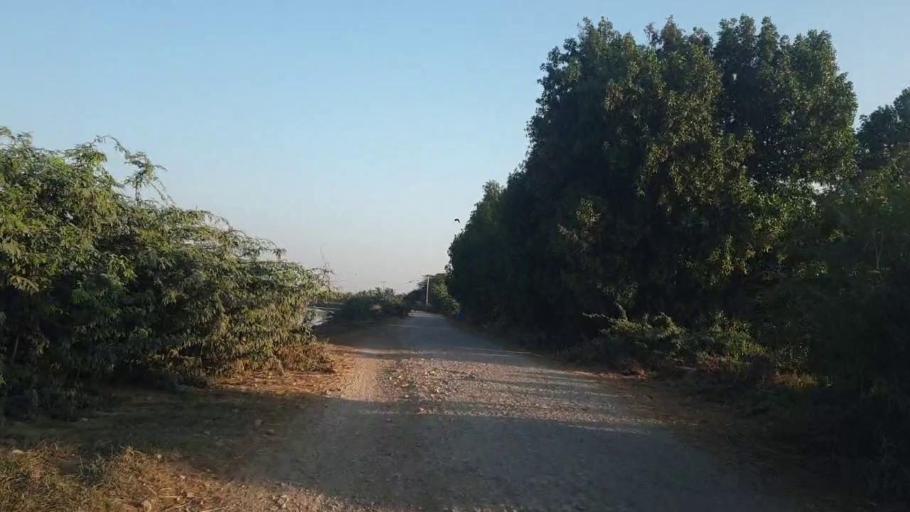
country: PK
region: Sindh
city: Mirpur Sakro
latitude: 24.4638
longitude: 67.5878
